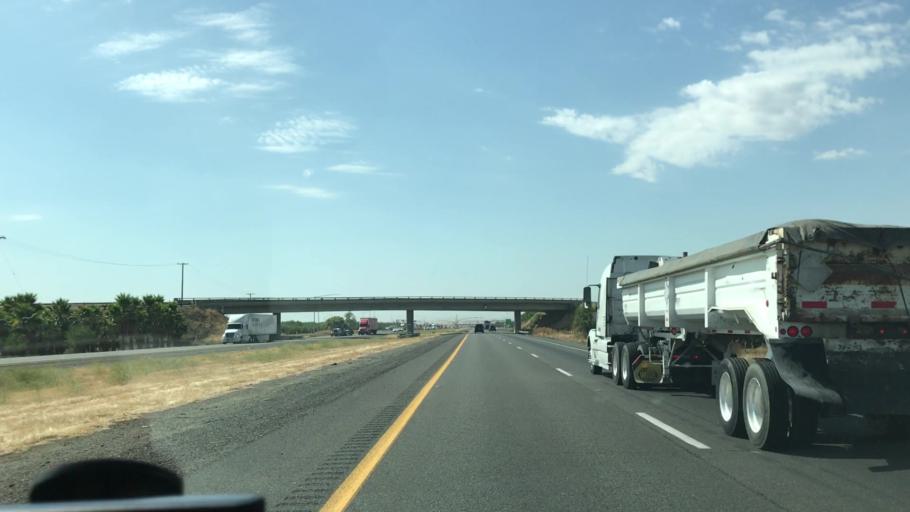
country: US
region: California
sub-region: Merced County
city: Gustine
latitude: 37.1330
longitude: -121.0344
